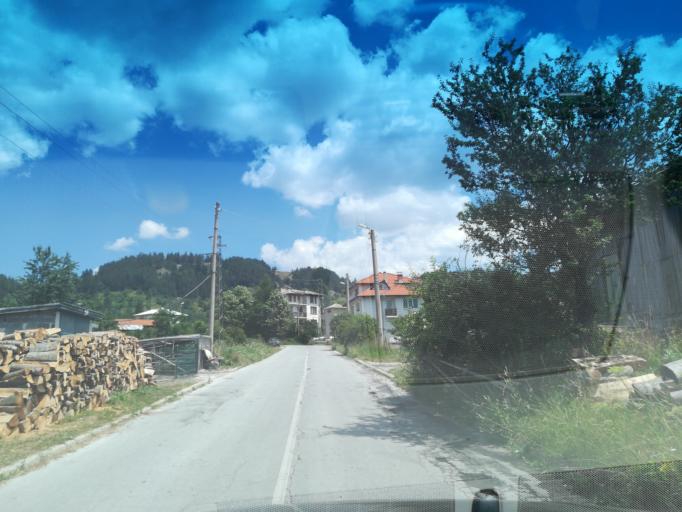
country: BG
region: Smolyan
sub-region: Obshtina Smolyan
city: Smolyan
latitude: 41.6620
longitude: 24.7729
